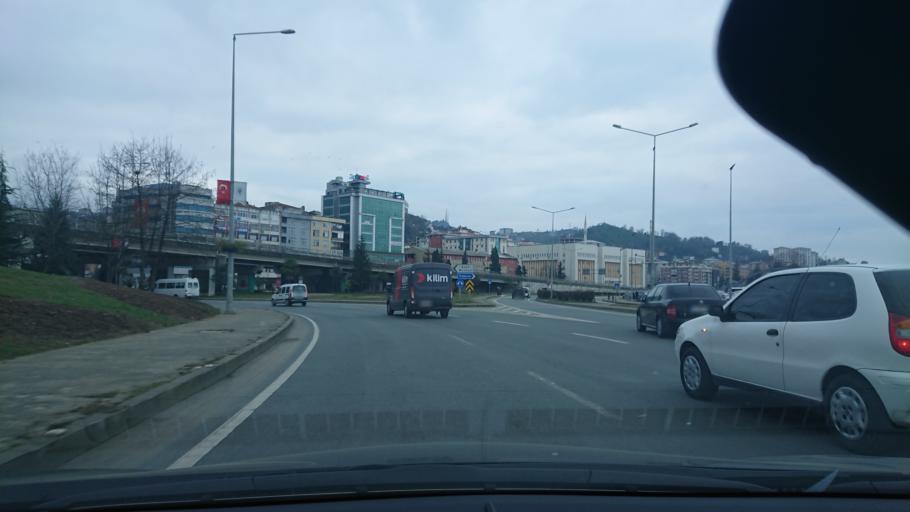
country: TR
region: Rize
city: Rize
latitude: 41.0275
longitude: 40.5196
